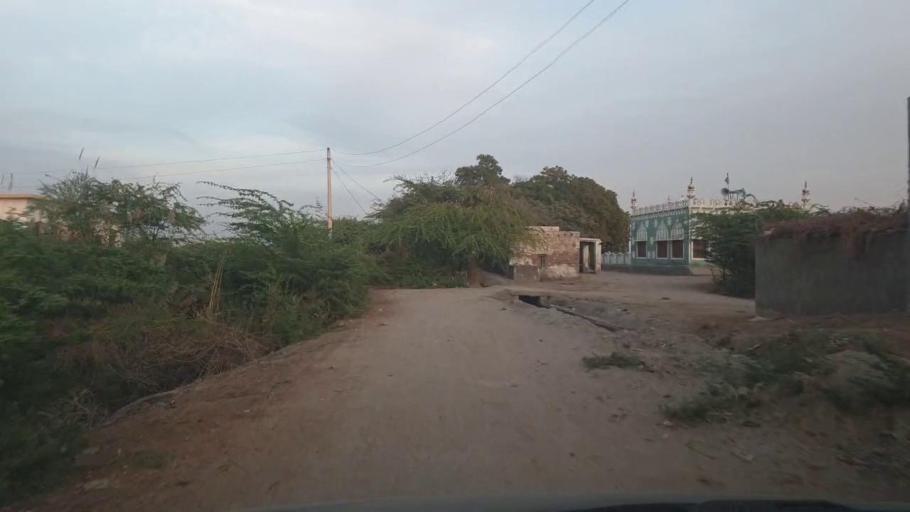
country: PK
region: Sindh
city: Kunri
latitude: 25.2241
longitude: 69.5418
